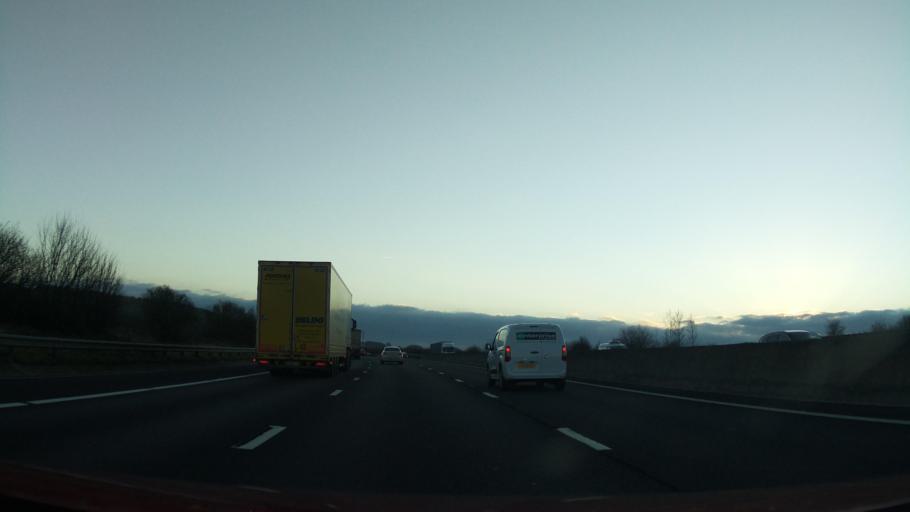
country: GB
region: England
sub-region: City and Borough of Leeds
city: Wetherby
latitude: 53.9199
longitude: -1.3845
